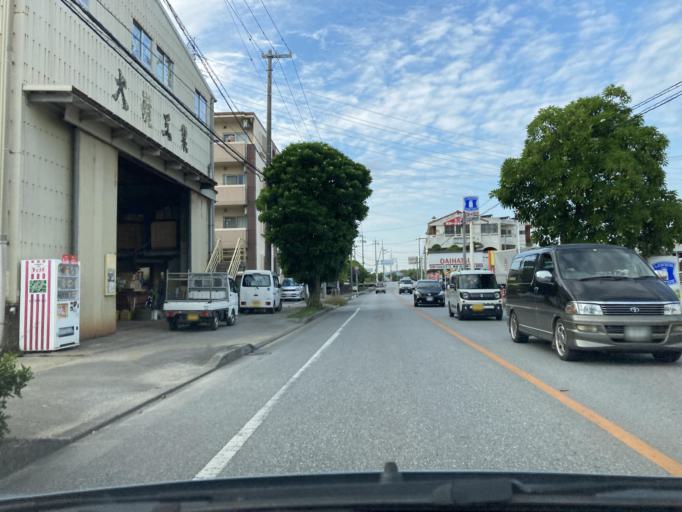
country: JP
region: Okinawa
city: Okinawa
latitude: 26.3683
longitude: 127.8156
